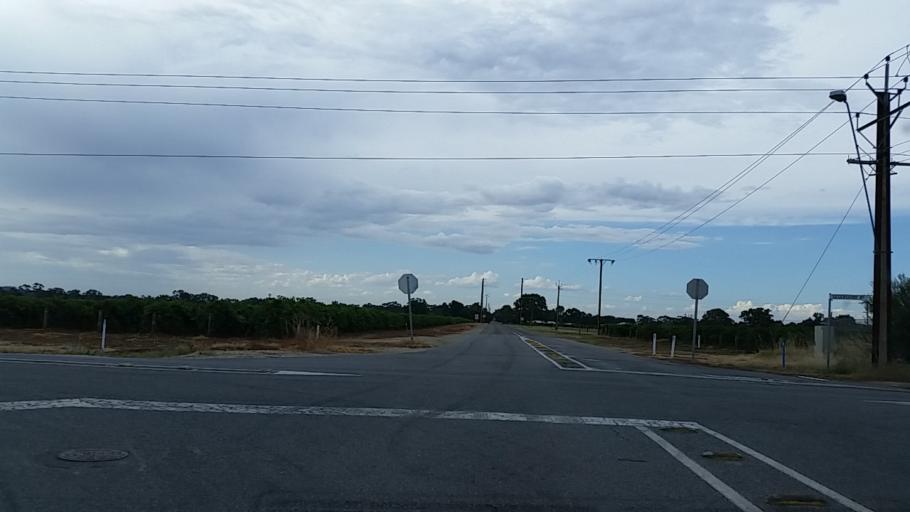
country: AU
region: South Australia
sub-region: Barossa
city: Angaston
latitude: -34.5052
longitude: 139.0087
